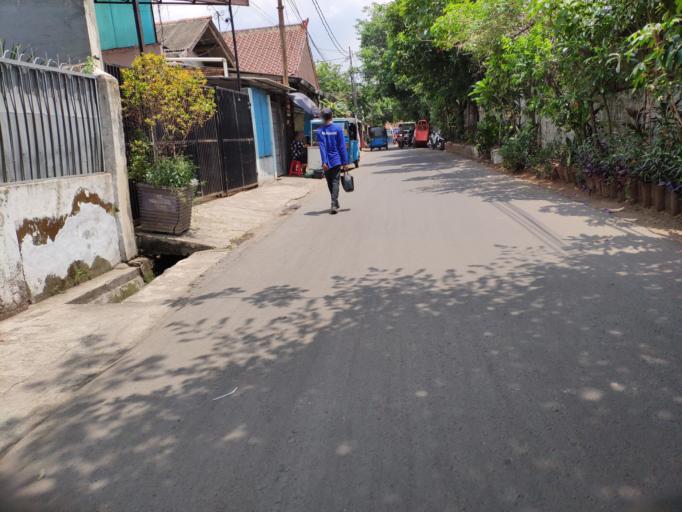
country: ID
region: Jakarta Raya
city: Jakarta
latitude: -6.2146
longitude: 106.8713
